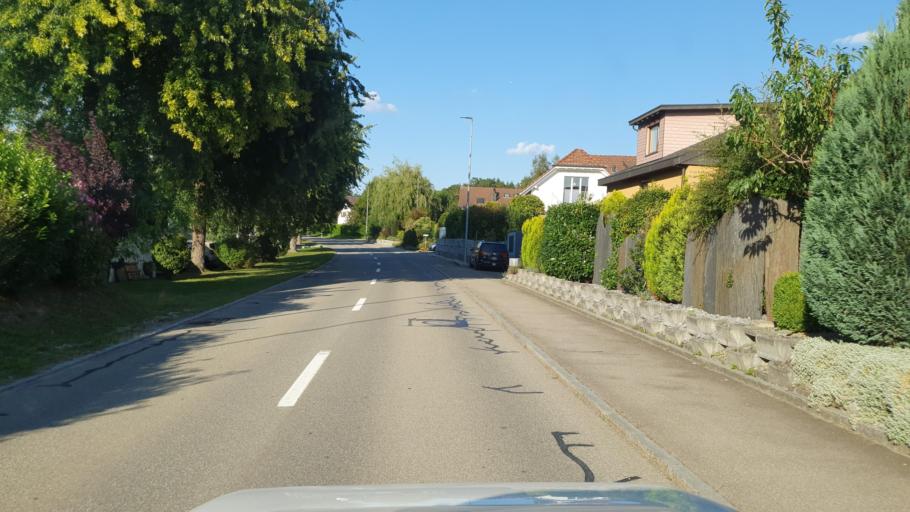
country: CH
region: Aargau
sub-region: Bezirk Muri
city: Waltenschwil
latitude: 47.3122
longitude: 8.3262
